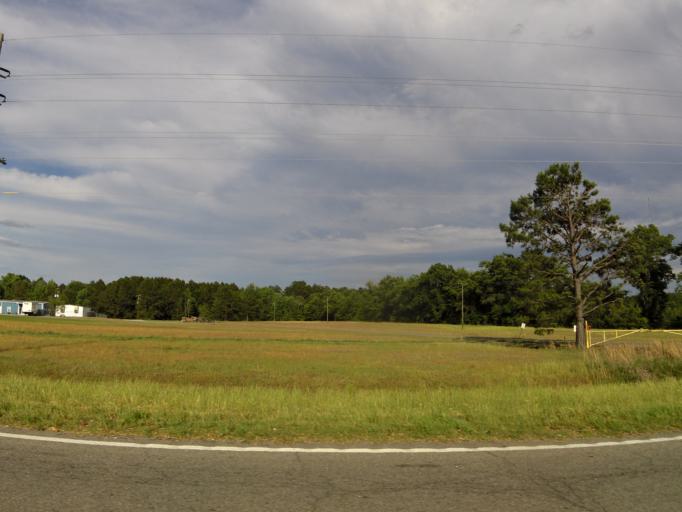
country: US
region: South Carolina
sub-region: Hampton County
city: Estill
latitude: 32.7794
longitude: -81.2407
